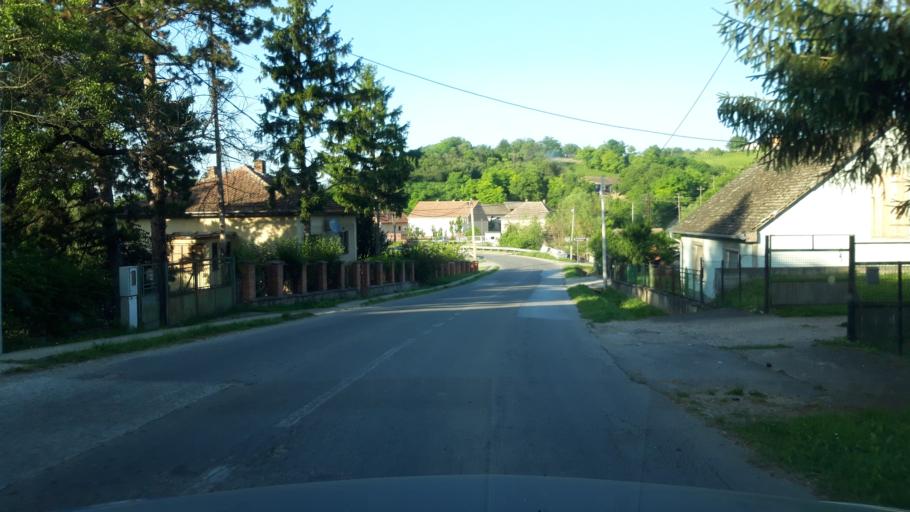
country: RS
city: Glozan
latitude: 45.2111
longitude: 19.6051
